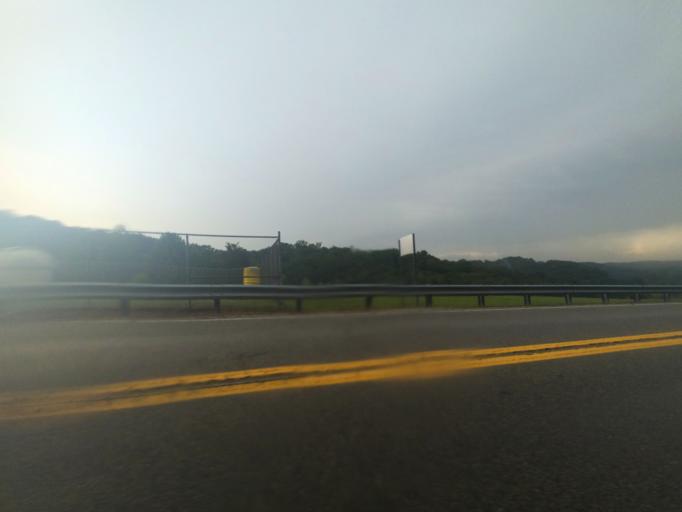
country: US
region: West Virginia
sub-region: Cabell County
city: Huntington
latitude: 38.3897
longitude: -82.3947
